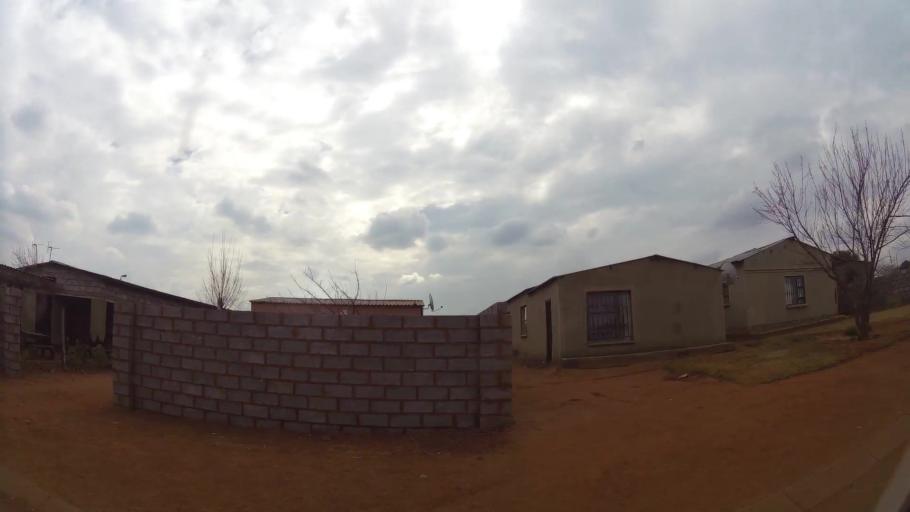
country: ZA
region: Gauteng
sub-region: Ekurhuleni Metropolitan Municipality
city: Germiston
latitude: -26.3814
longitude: 28.1222
